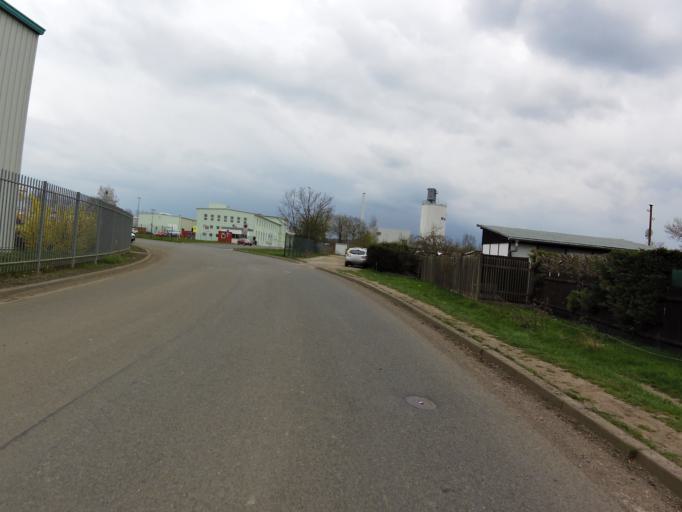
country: DE
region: Thuringia
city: Gotha
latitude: 50.9531
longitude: 10.7201
